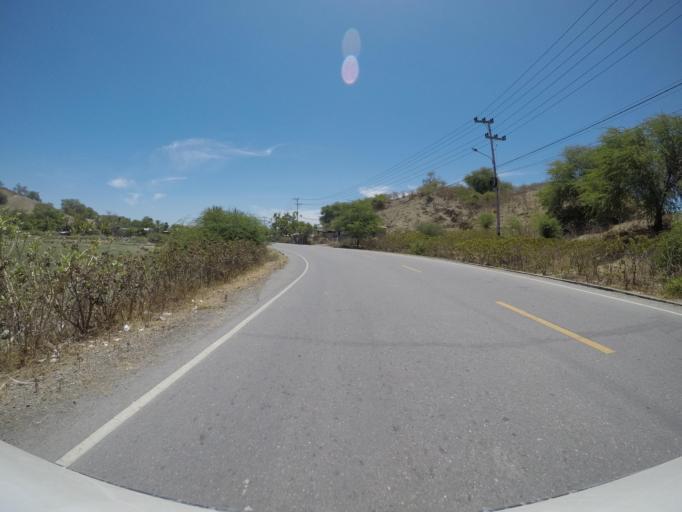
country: TL
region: Manatuto
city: Manatuto
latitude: -8.5241
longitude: 126.0061
